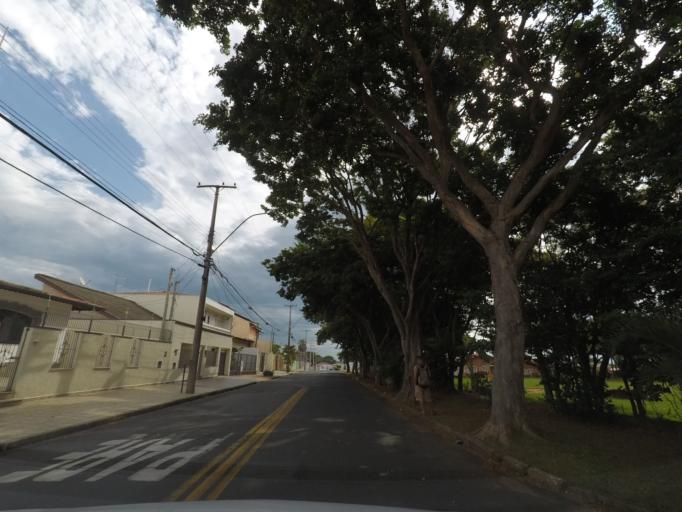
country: BR
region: Sao Paulo
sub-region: Campinas
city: Campinas
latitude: -22.8879
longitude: -47.1060
